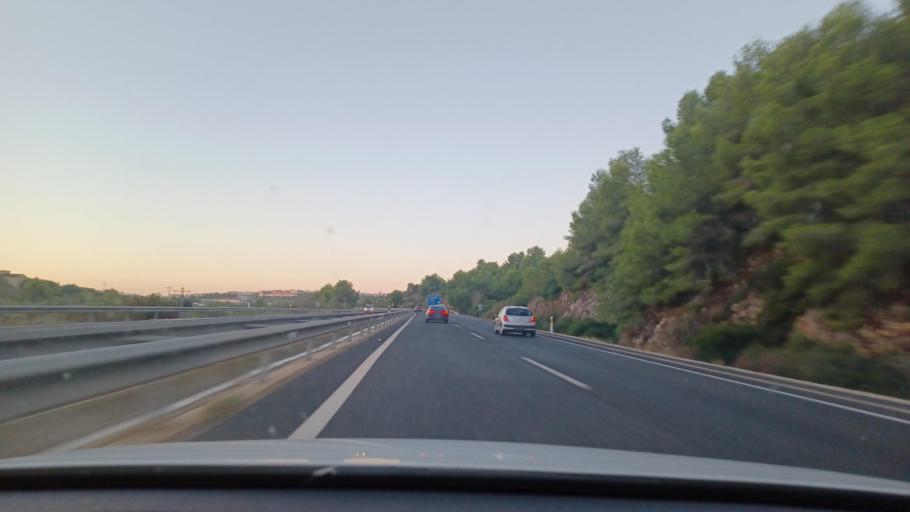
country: ES
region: Valencia
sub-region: Provincia de Alicante
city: Senija
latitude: 38.7384
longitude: 0.0527
